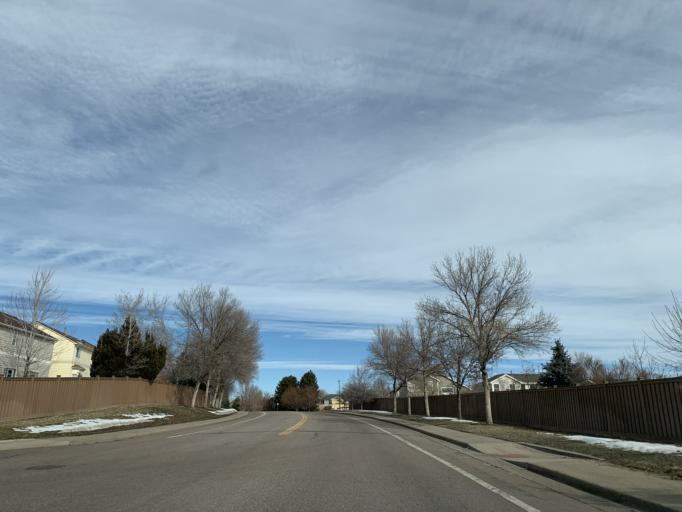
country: US
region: Colorado
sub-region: Douglas County
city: Carriage Club
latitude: 39.5383
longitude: -104.9295
